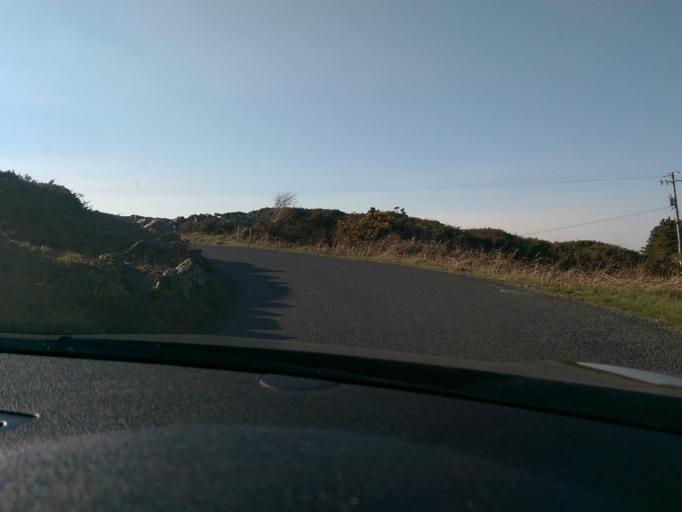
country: IE
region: Connaught
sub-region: County Galway
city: Clifden
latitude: 53.3747
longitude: -9.8326
